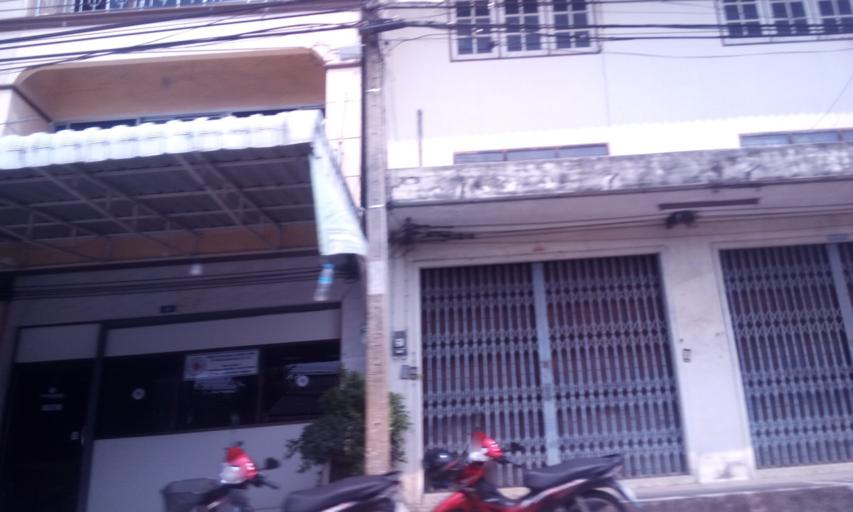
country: TH
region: Chon Buri
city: Phanat Nikhom
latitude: 13.4388
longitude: 101.1792
